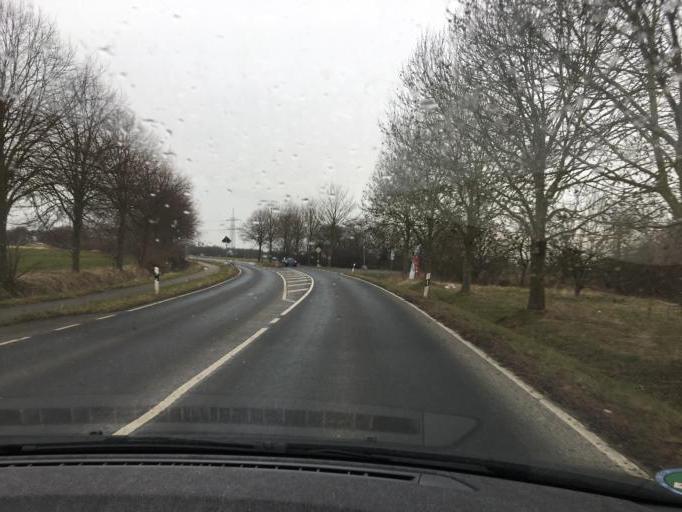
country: DE
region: North Rhine-Westphalia
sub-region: Regierungsbezirk Koln
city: Bergheim
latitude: 50.9366
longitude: 6.6250
